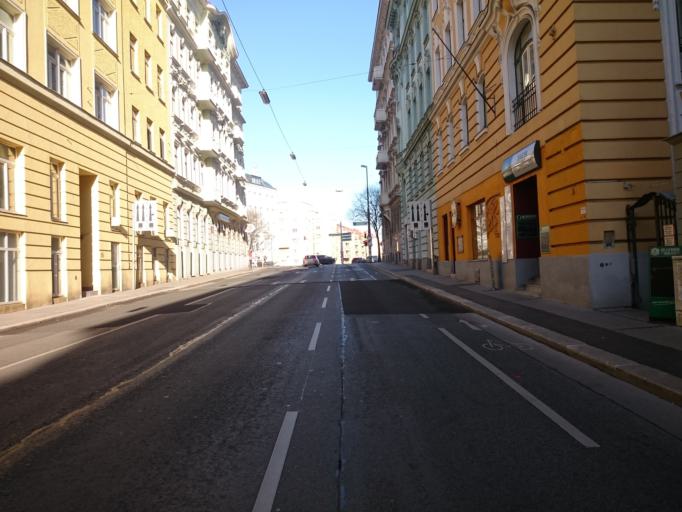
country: AT
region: Vienna
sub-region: Wien Stadt
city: Vienna
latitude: 48.2320
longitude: 16.3561
